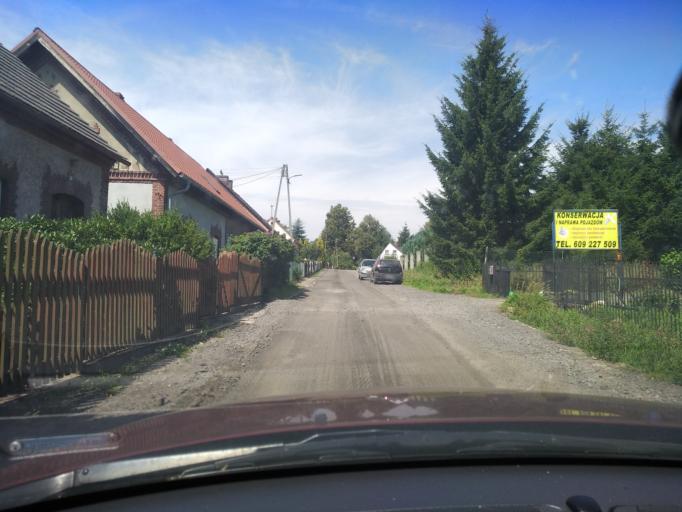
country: PL
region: Lower Silesian Voivodeship
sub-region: Powiat lwowecki
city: Mirsk
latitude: 50.9802
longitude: 15.3445
